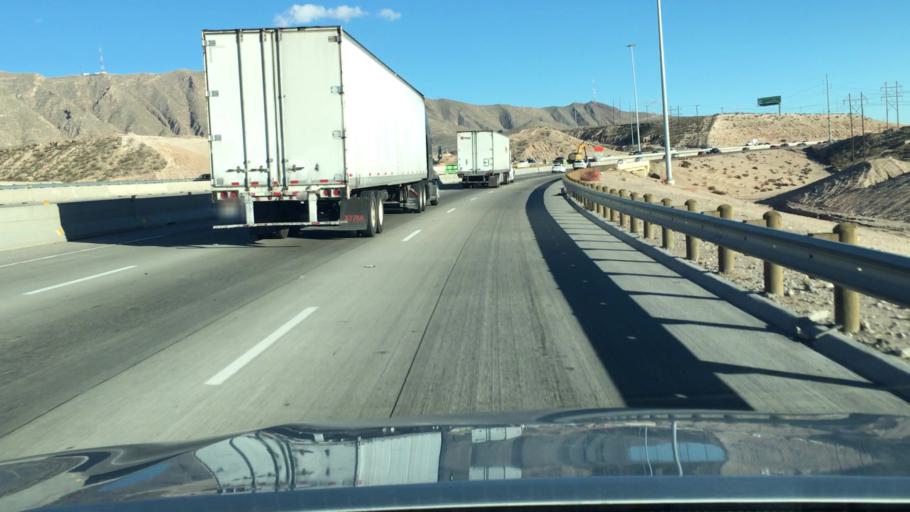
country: US
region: New Mexico
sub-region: Dona Ana County
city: Sunland Park
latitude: 31.8090
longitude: -106.5275
